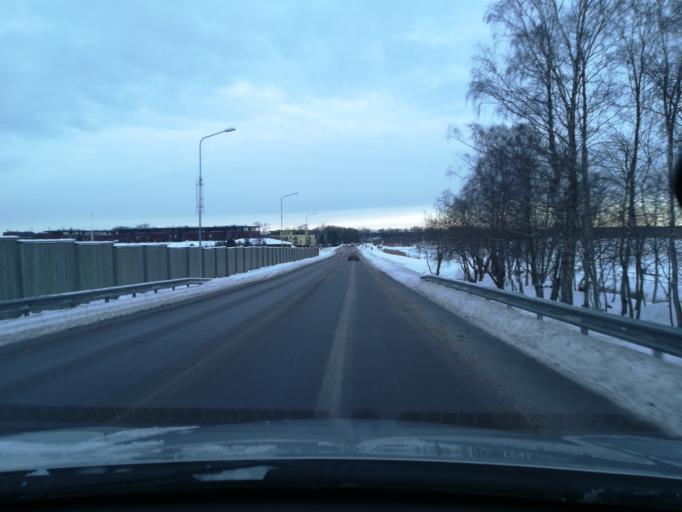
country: EE
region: Harju
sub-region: Harku vald
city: Tabasalu
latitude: 59.4306
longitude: 24.5603
